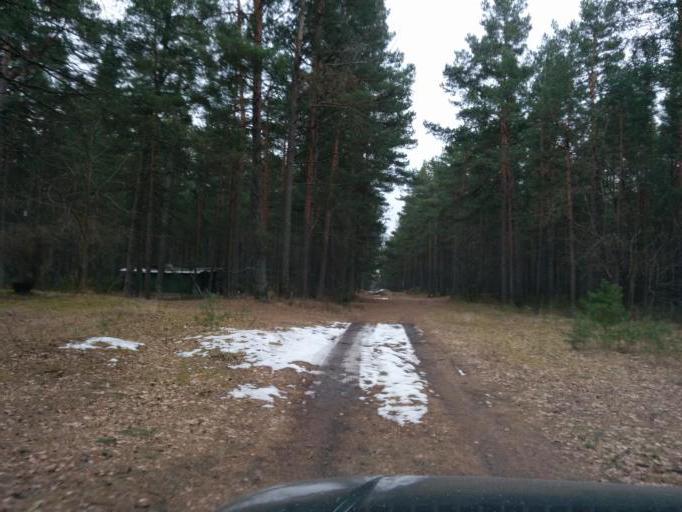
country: LV
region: Babite
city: Pinki
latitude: 56.9894
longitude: 23.8859
